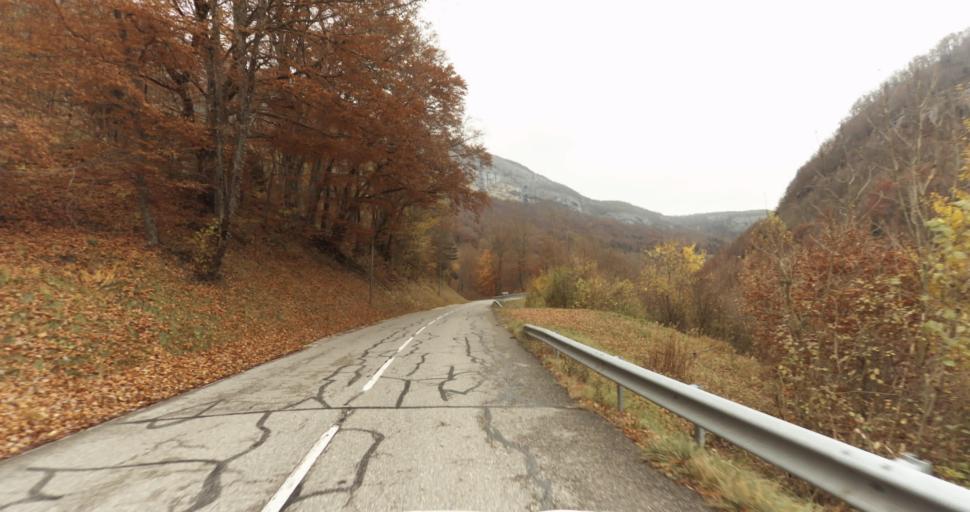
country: FR
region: Rhone-Alpes
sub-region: Departement de la Haute-Savoie
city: Gruffy
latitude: 45.7480
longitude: 6.0902
